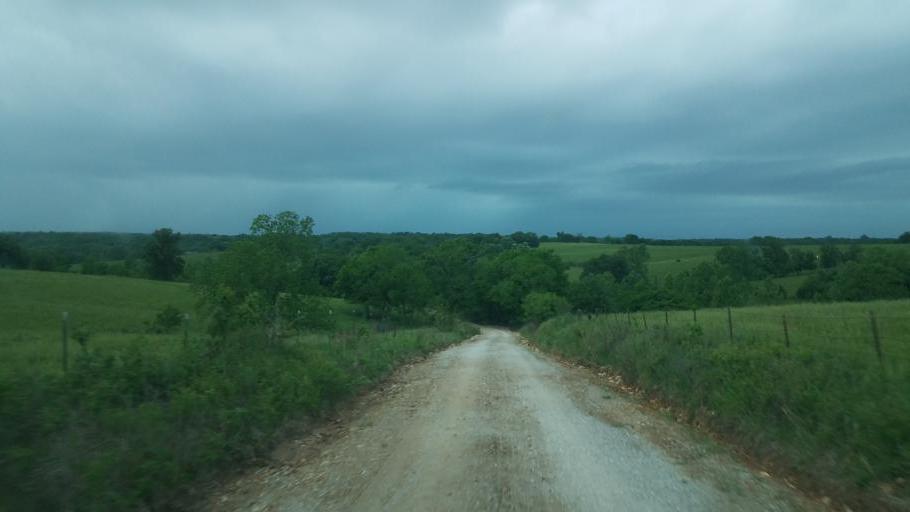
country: US
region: Missouri
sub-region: Moniteau County
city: California
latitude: 38.7521
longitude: -92.6167
